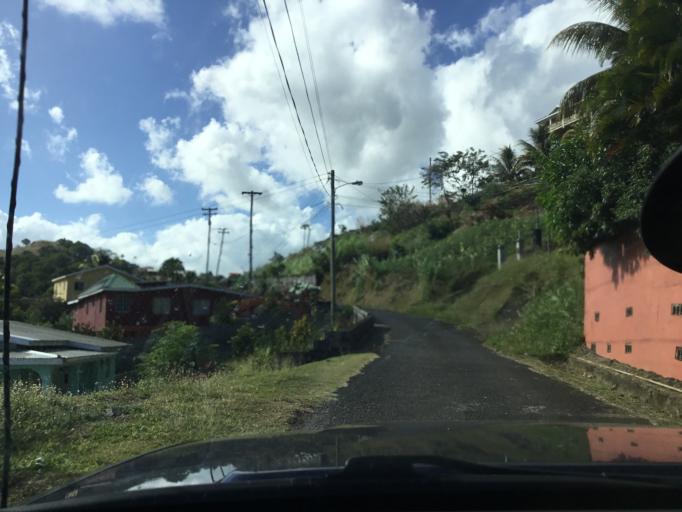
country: VC
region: Saint George
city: Kingstown
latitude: 13.1466
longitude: -61.1780
